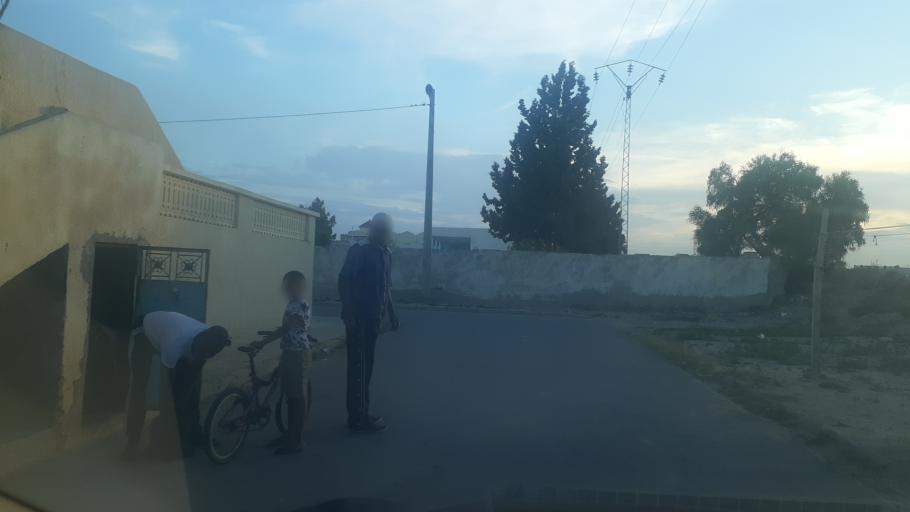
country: TN
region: Qabis
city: Gabes
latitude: 33.9333
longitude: 10.0421
